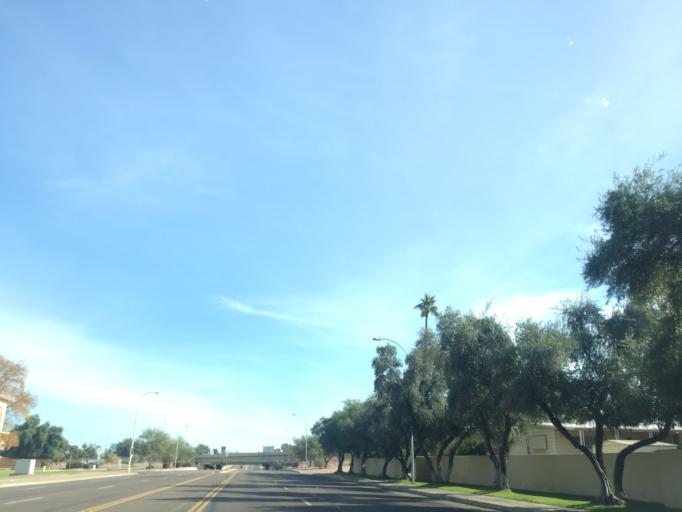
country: US
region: Arizona
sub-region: Maricopa County
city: Guadalupe
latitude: 33.3928
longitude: -111.9712
